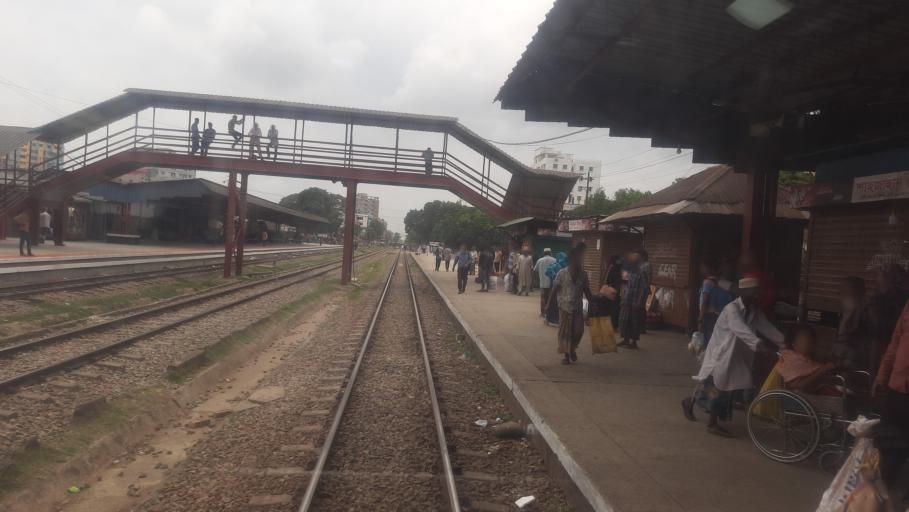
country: BD
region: Chittagong
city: Feni
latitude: 23.0135
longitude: 91.4034
